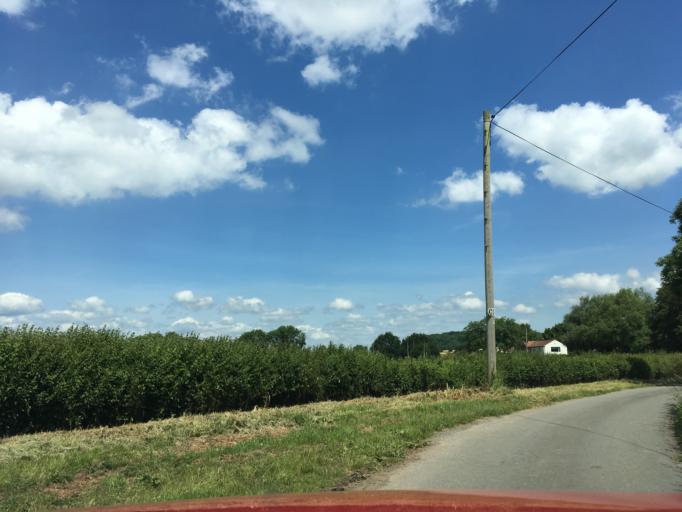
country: GB
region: England
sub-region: South Gloucestershire
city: Hill
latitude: 51.6372
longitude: -2.5047
